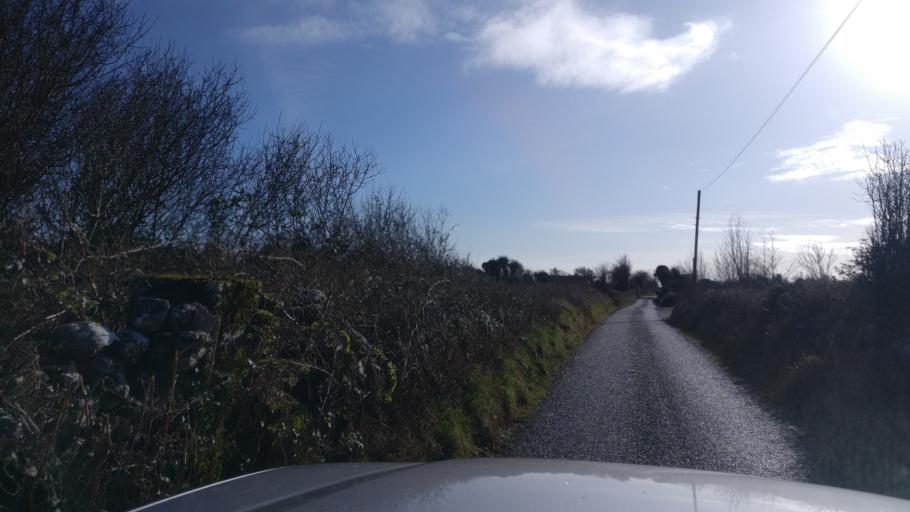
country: IE
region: Connaught
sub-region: County Galway
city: Athenry
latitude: 53.2400
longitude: -8.7816
